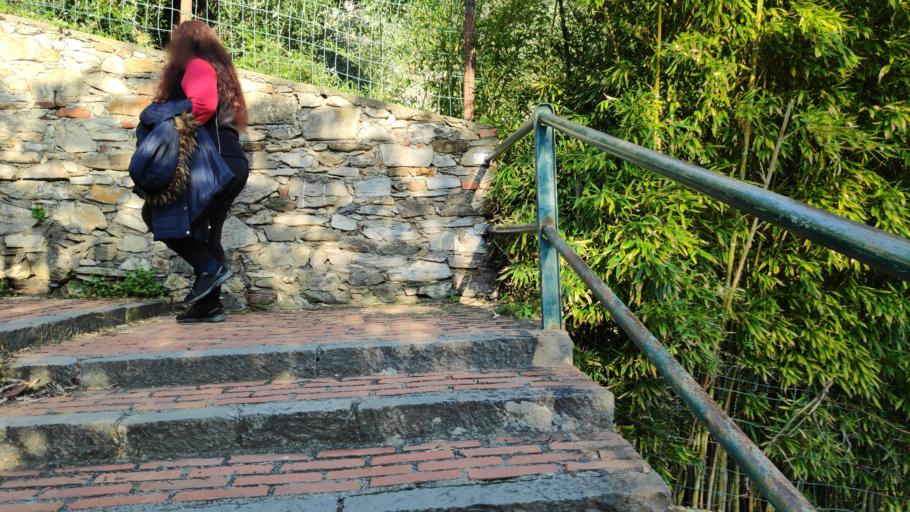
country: IT
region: Liguria
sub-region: Provincia di La Spezia
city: Vernazza
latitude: 44.1199
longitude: 9.7113
